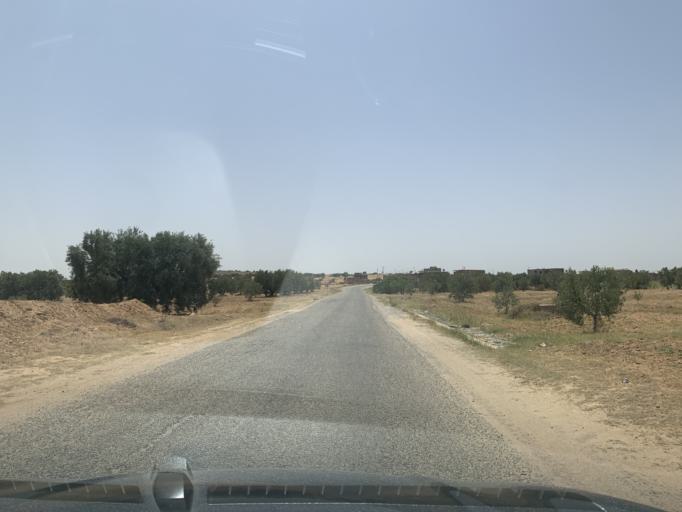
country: TN
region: Al Mahdiyah
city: Shurban
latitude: 35.1626
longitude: 10.2428
